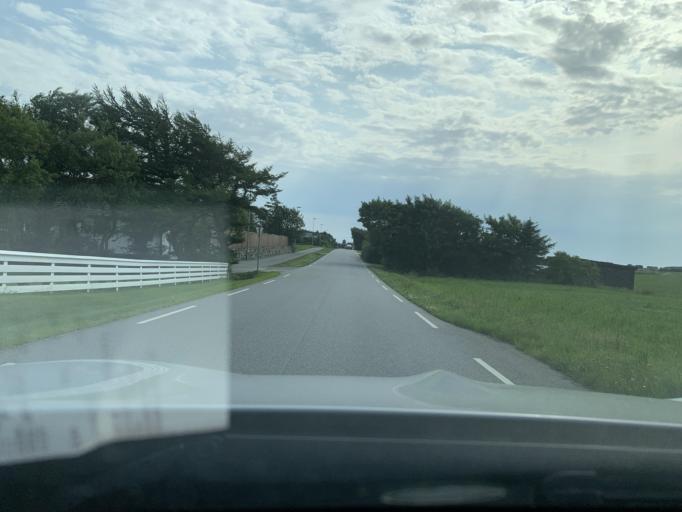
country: NO
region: Rogaland
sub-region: Time
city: Bryne
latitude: 58.7223
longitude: 5.5758
